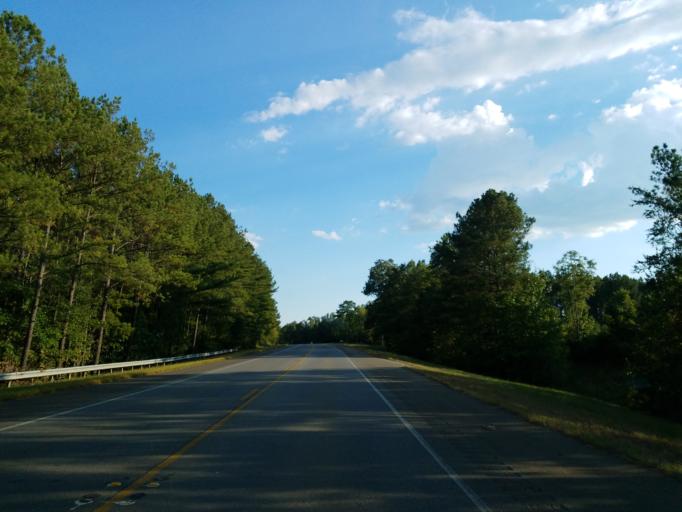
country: US
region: Georgia
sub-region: Murray County
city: Chatsworth
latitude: 34.6561
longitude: -84.7200
